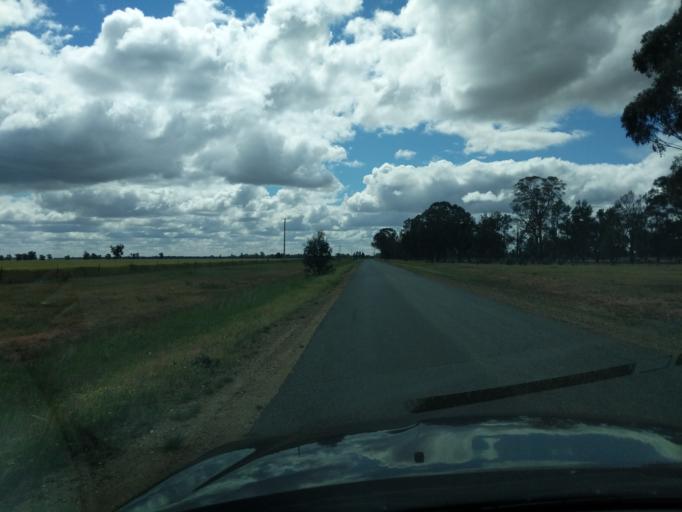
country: AU
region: New South Wales
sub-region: Coolamon
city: Coolamon
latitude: -34.8660
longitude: 146.8968
